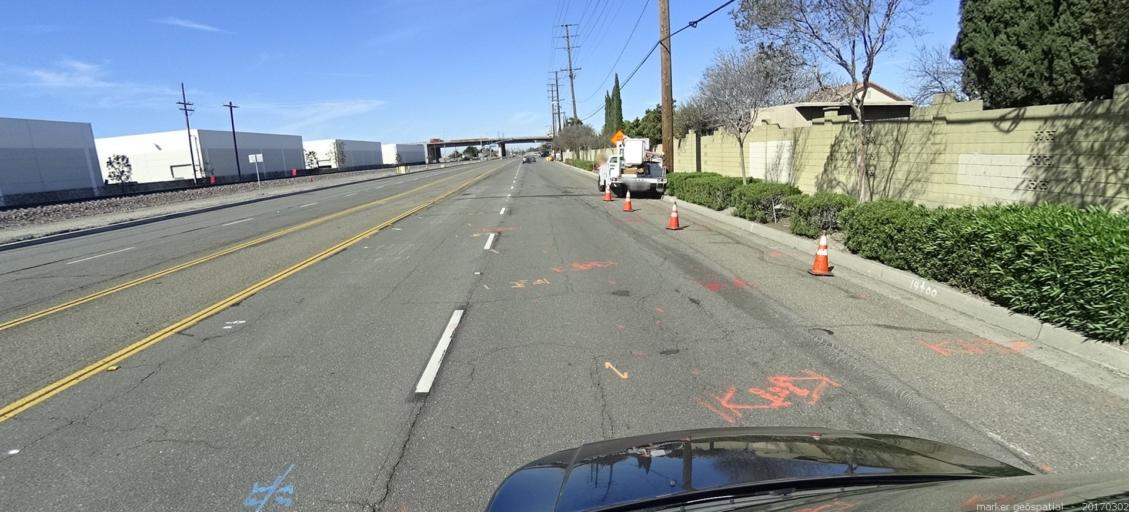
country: US
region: California
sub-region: Orange County
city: Yorba Linda
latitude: 33.8664
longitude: -117.8153
